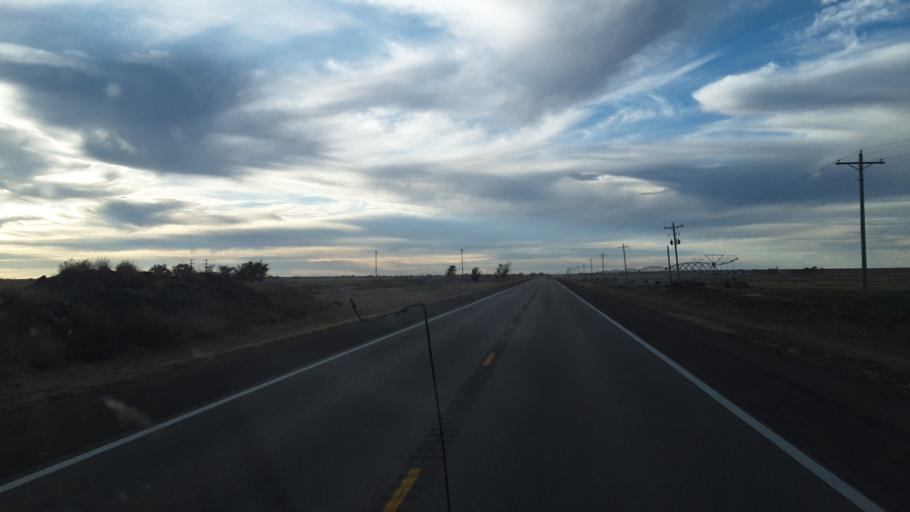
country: US
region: Kansas
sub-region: Hamilton County
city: Syracuse
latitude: 38.0161
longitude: -101.8882
